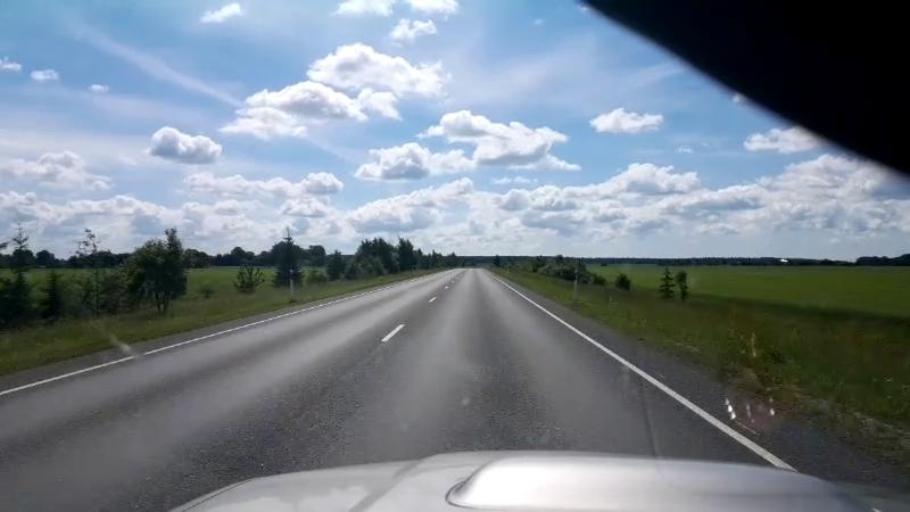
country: EE
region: Jaervamaa
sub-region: Jaerva-Jaani vald
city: Jarva-Jaani
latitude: 59.1559
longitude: 25.7662
